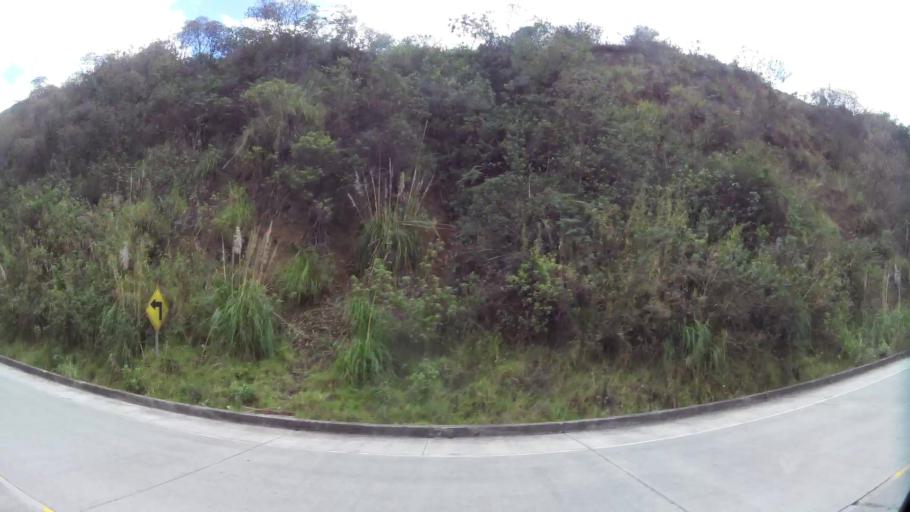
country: EC
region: Azuay
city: Cuenca
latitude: -3.1380
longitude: -79.1210
